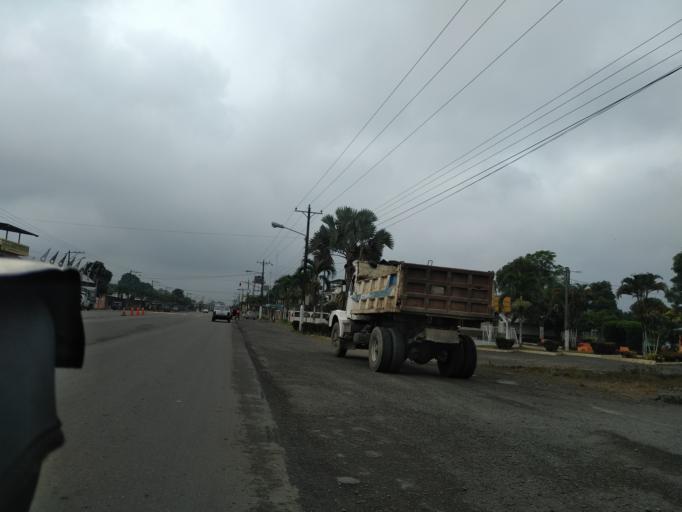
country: EC
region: Cotopaxi
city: La Mana
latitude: -0.9444
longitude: -79.3264
